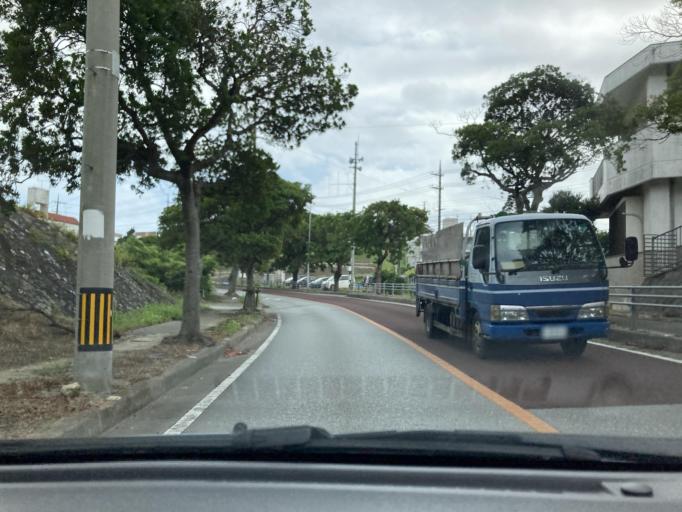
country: JP
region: Okinawa
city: Ginowan
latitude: 26.2630
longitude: 127.7749
